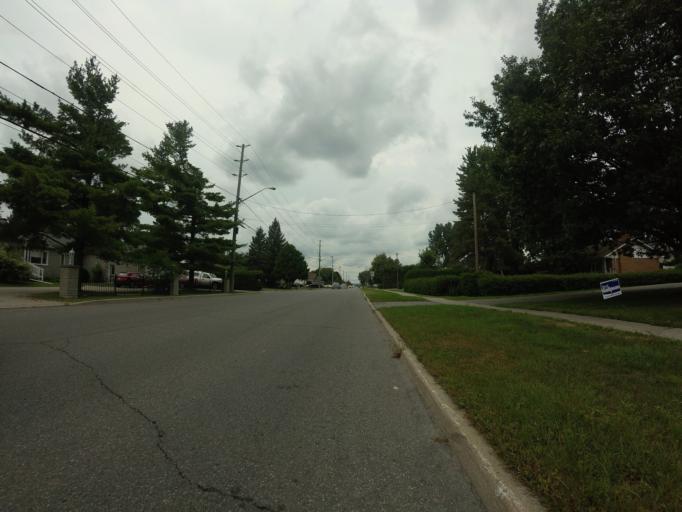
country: CA
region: Quebec
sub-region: Outaouais
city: Gatineau
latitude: 45.4653
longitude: -75.5182
